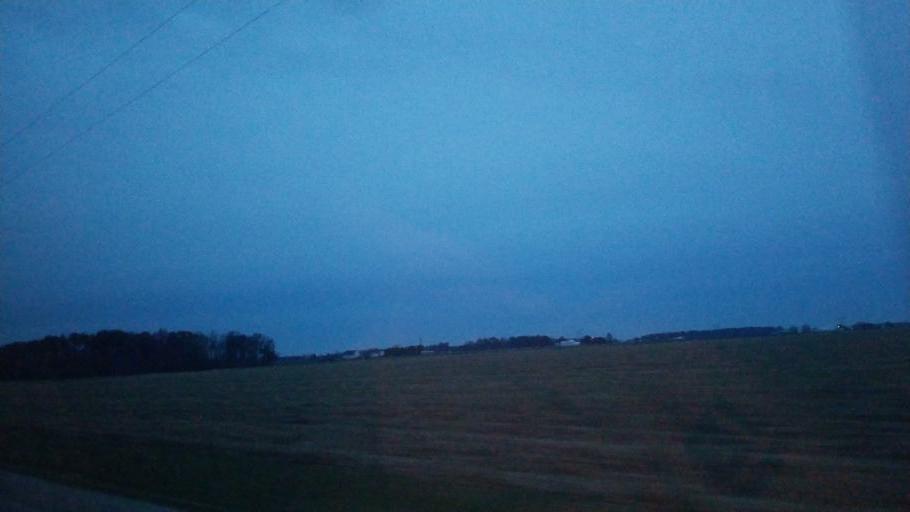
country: US
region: Indiana
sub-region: Adams County
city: Berne
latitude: 40.7027
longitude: -84.9940
